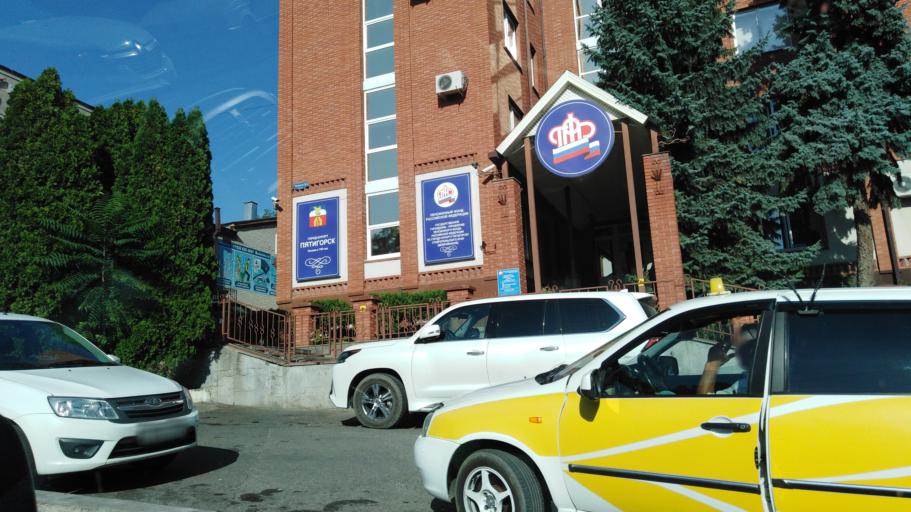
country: RU
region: Stavropol'skiy
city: Pyatigorsk
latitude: 44.0479
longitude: 43.0686
